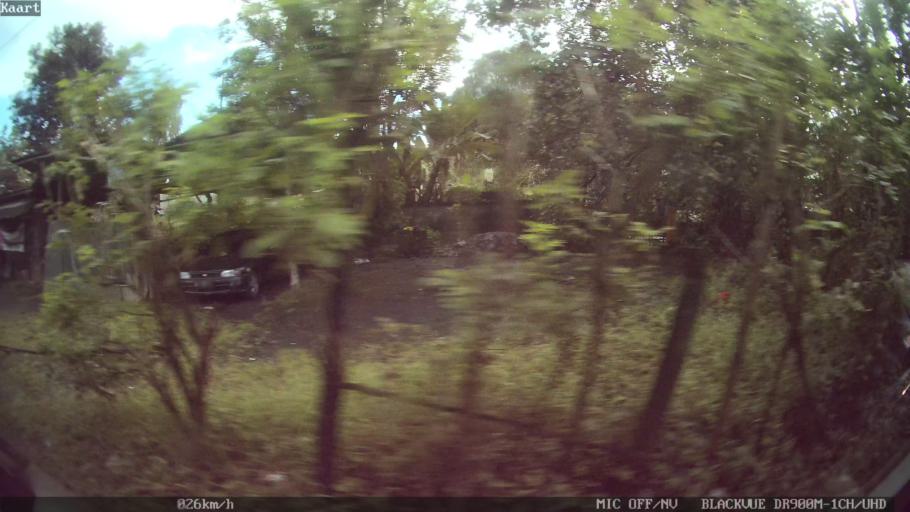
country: ID
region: Bali
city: Banjar Tebongkang
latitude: -8.5410
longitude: 115.2598
